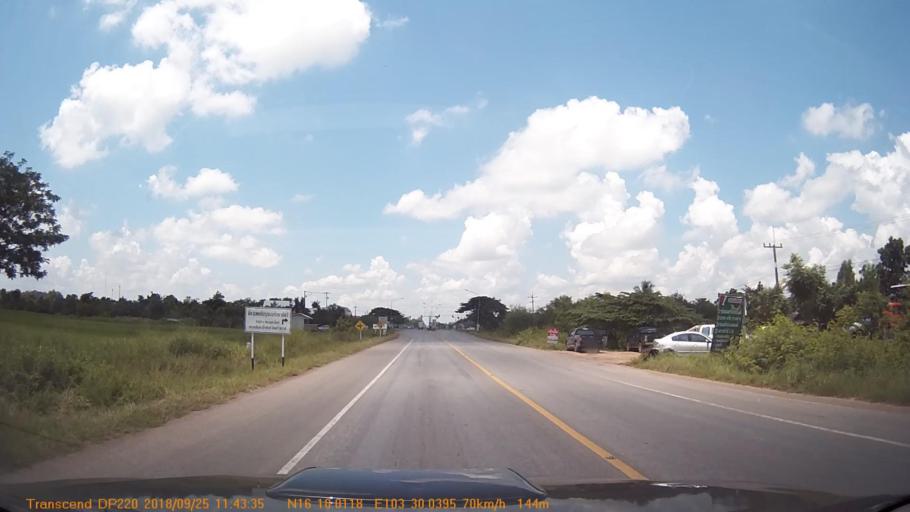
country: TH
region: Kalasin
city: Khong Chai
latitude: 16.3002
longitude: 103.5007
